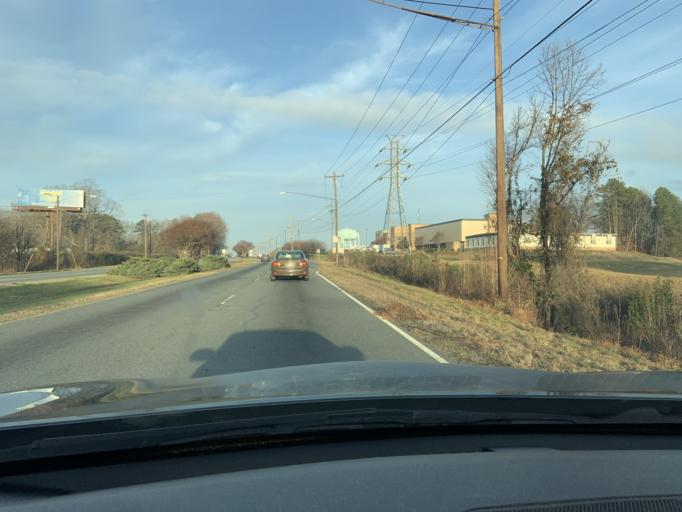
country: US
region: North Carolina
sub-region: Mecklenburg County
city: Charlotte
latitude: 35.2752
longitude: -80.8881
